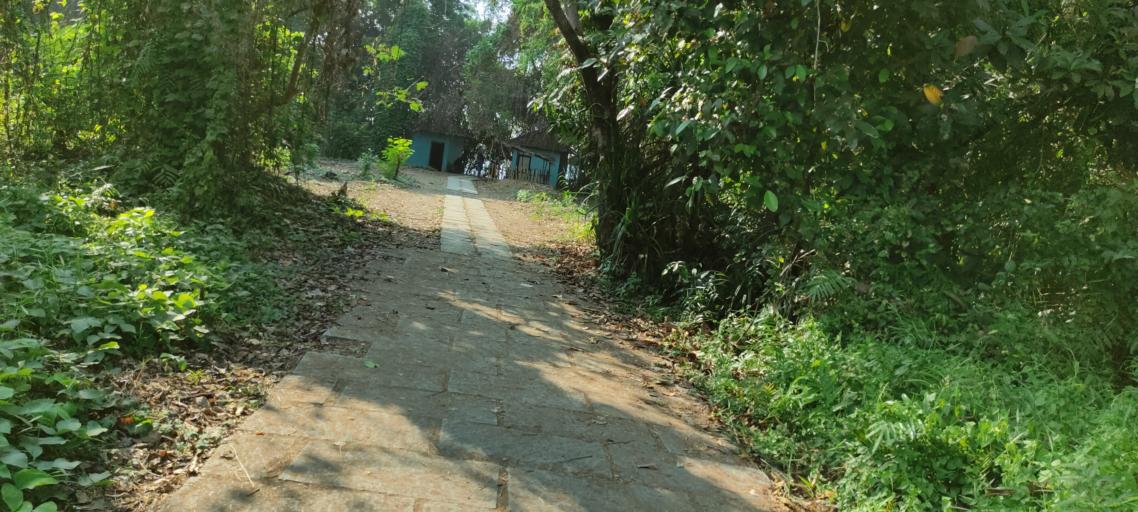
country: IN
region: Kerala
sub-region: Alappuzha
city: Shertallai
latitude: 9.6194
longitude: 76.3836
